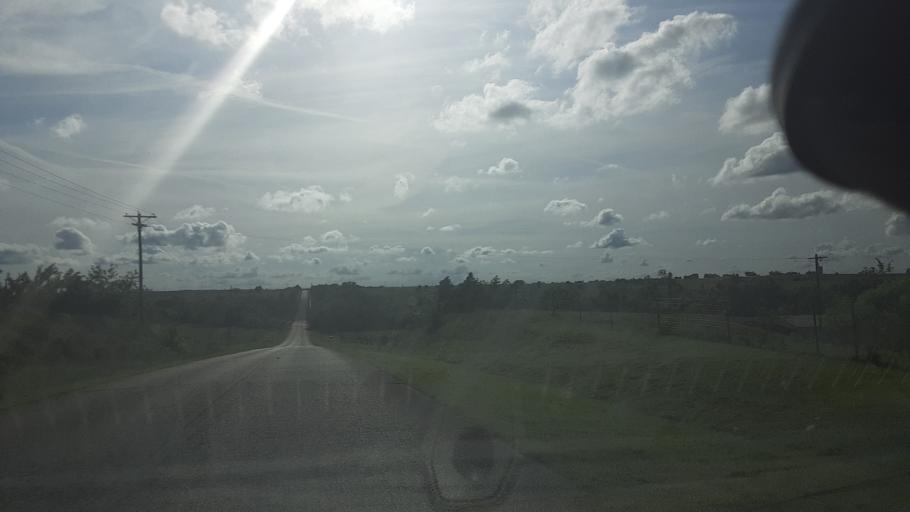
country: US
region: Oklahoma
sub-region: Logan County
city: Langston
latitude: 36.0578
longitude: -97.3846
